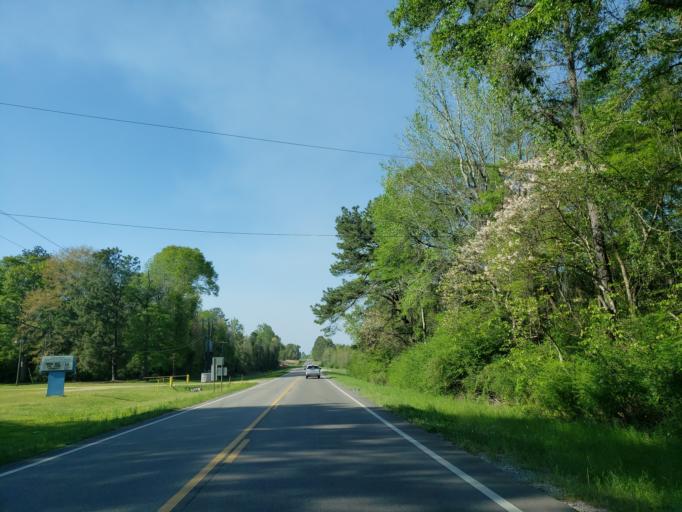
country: US
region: Mississippi
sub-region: Perry County
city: Richton
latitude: 31.3603
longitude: -88.9355
